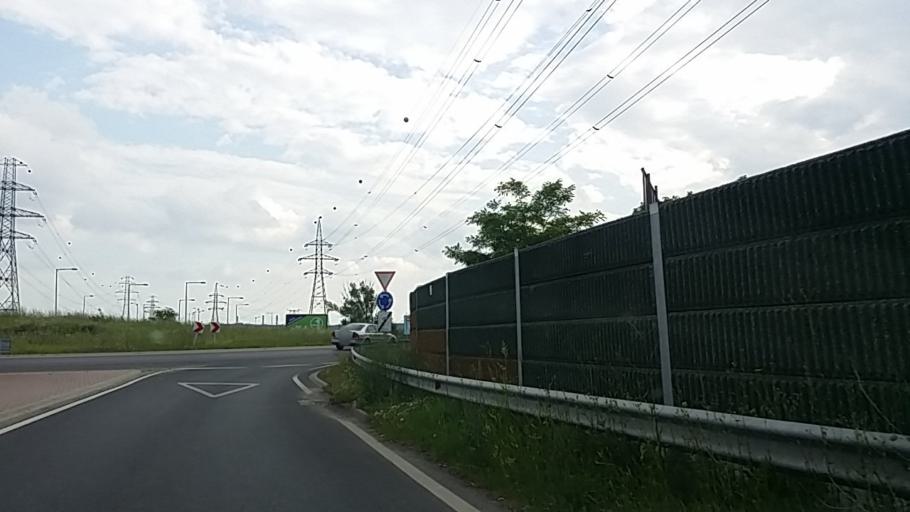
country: HU
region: Pest
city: Diosd
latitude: 47.3837
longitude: 18.9552
